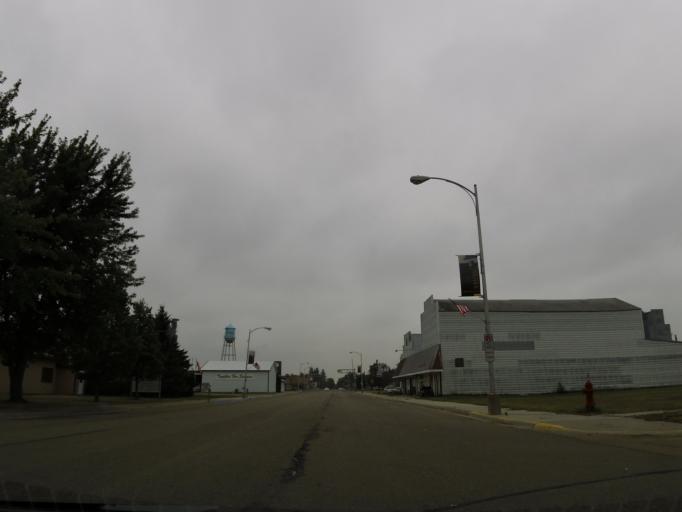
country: US
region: Minnesota
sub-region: Marshall County
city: Warren
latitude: 48.4508
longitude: -96.8710
